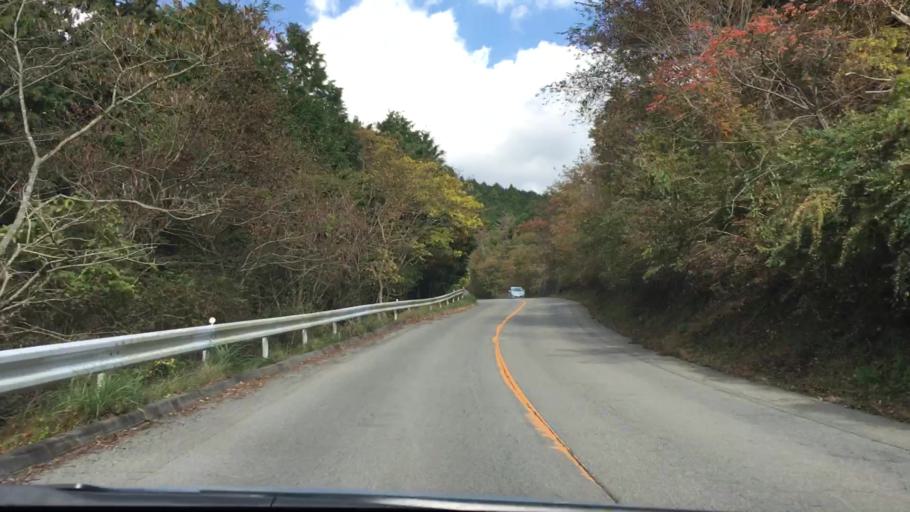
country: JP
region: Shizuoka
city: Gotemba
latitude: 35.3842
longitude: 138.9437
